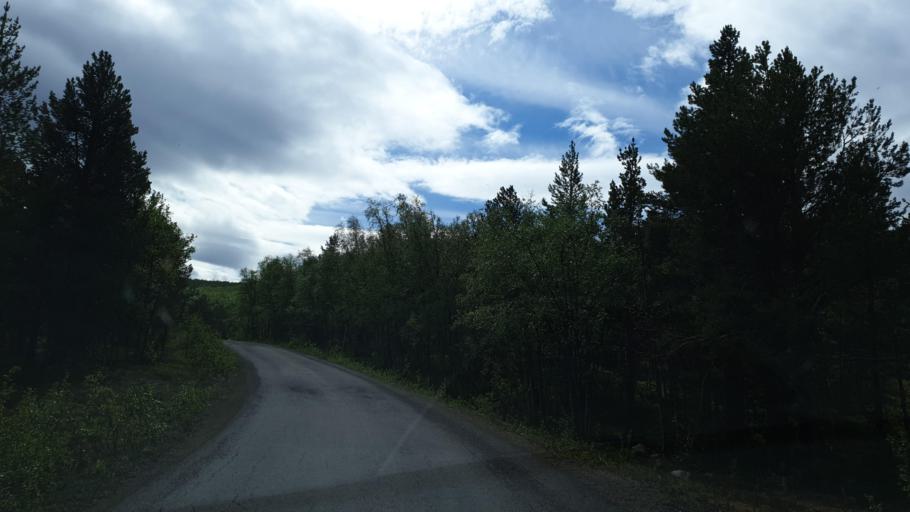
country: SE
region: Norrbotten
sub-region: Kiruna Kommun
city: Kiruna
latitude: 68.2221
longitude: 19.7137
